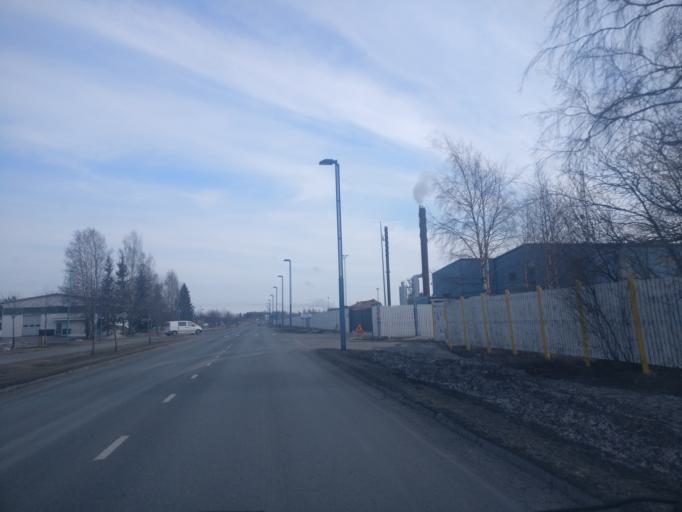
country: FI
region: Lapland
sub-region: Kemi-Tornio
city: Kemi
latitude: 65.7363
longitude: 24.5816
